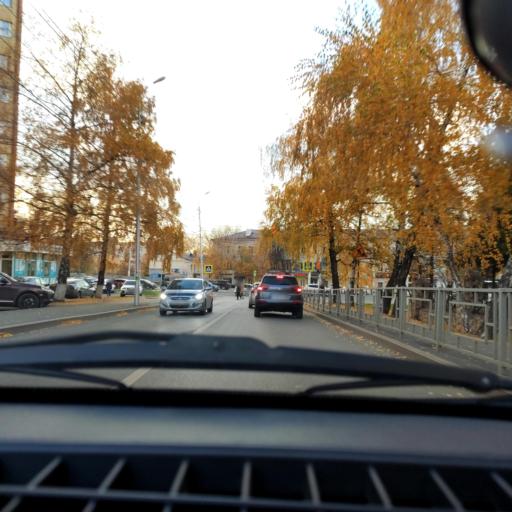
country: RU
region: Bashkortostan
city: Ufa
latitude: 54.7211
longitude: 56.0123
